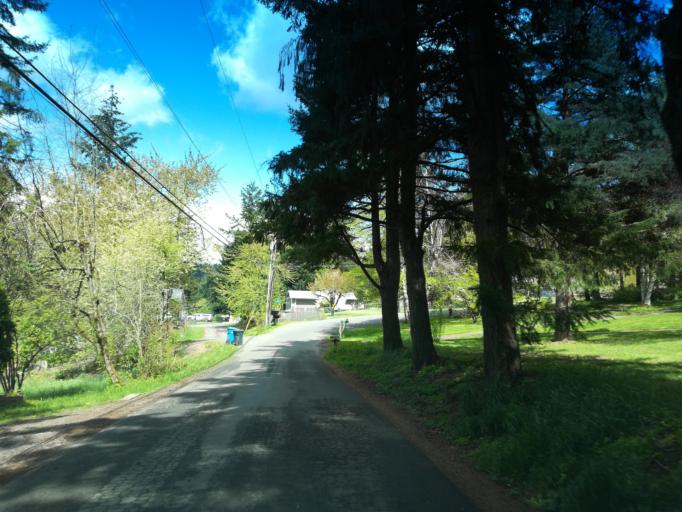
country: US
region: Oregon
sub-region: Clackamas County
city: Damascus
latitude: 45.4274
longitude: -122.4602
